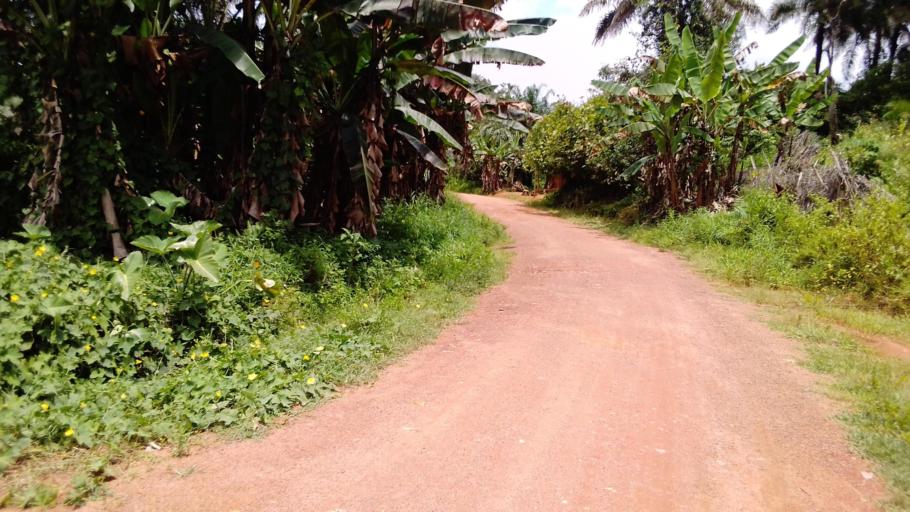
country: SL
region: Eastern Province
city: Koidu
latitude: 8.6732
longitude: -10.9360
